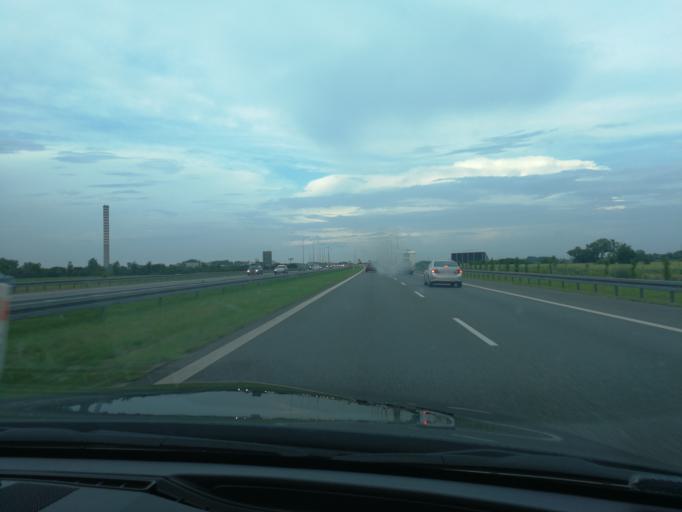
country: PL
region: Masovian Voivodeship
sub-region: Powiat pruszkowski
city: Brwinow
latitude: 52.1613
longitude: 20.7202
